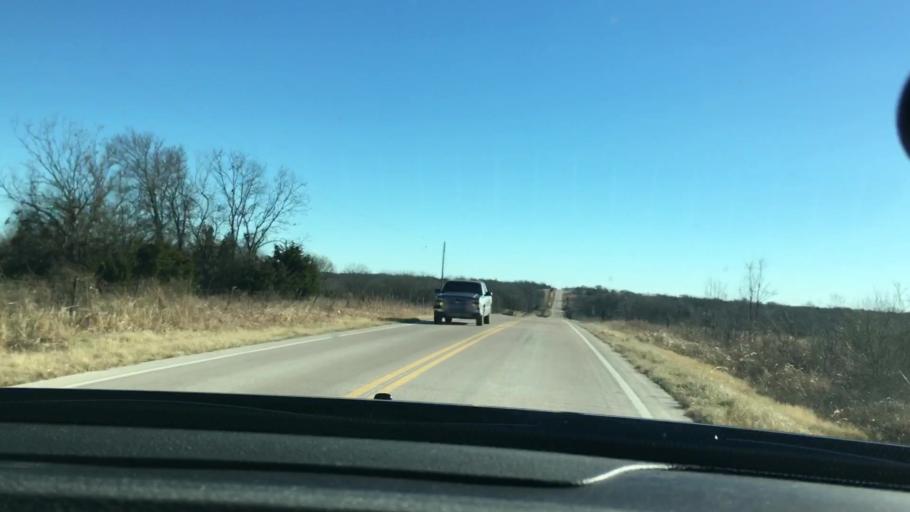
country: US
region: Oklahoma
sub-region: Johnston County
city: Tishomingo
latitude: 34.1144
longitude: -96.6452
